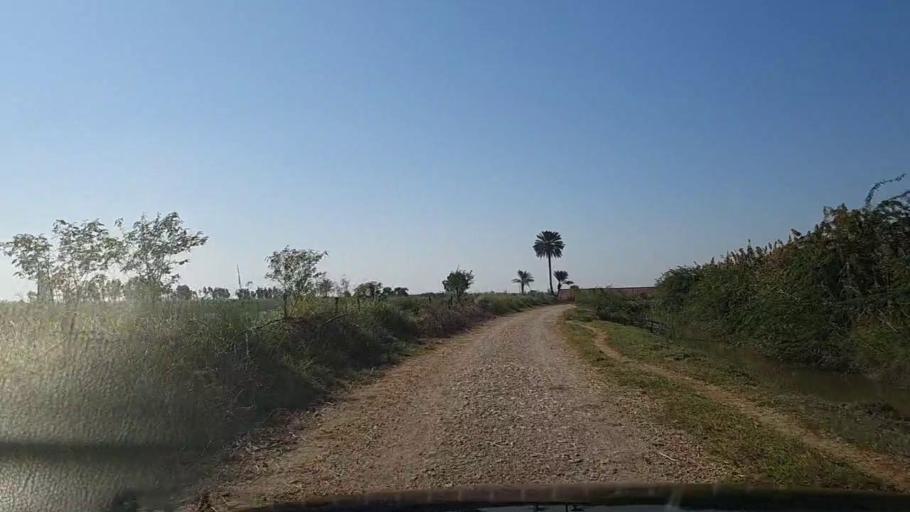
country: PK
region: Sindh
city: Thatta
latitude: 24.7046
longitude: 67.9083
